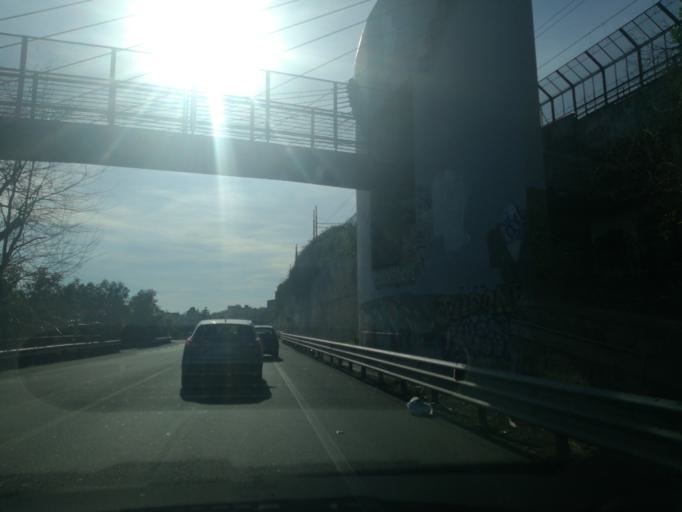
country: IT
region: Sicily
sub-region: Catania
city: Acireale
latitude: 37.6124
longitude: 15.1709
